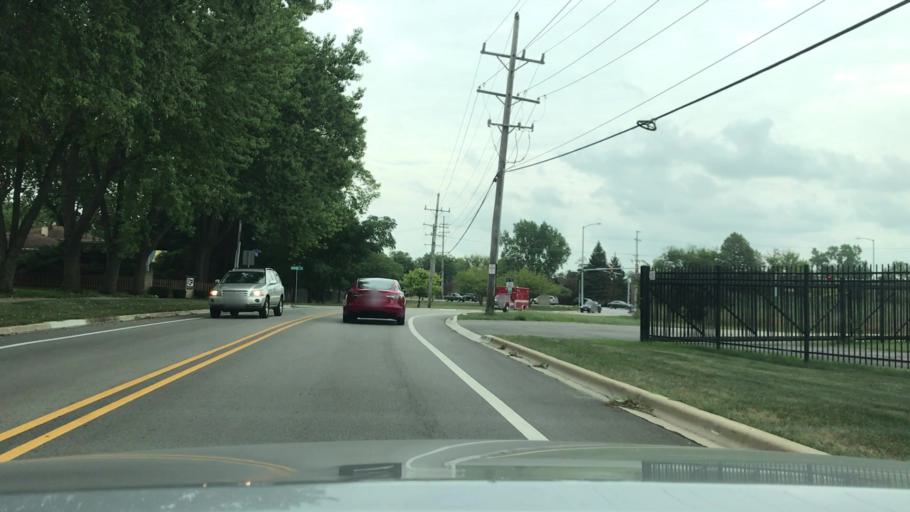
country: US
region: Illinois
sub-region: DuPage County
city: Darien
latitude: 41.7443
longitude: -87.9895
